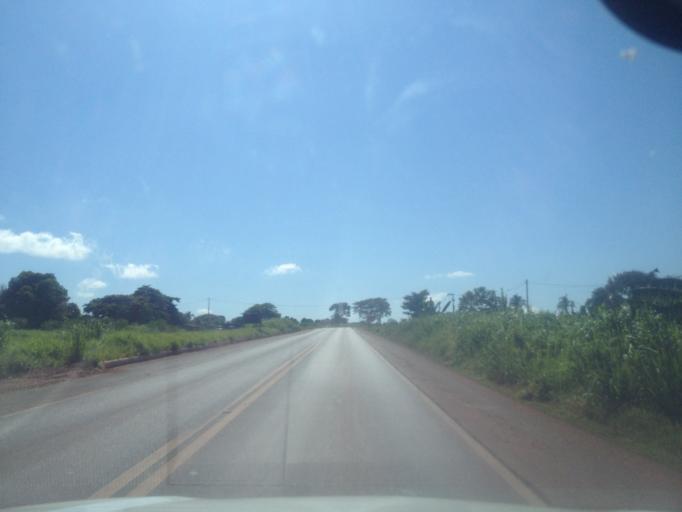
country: BR
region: Minas Gerais
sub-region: Santa Vitoria
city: Santa Vitoria
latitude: -19.0464
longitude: -50.4927
